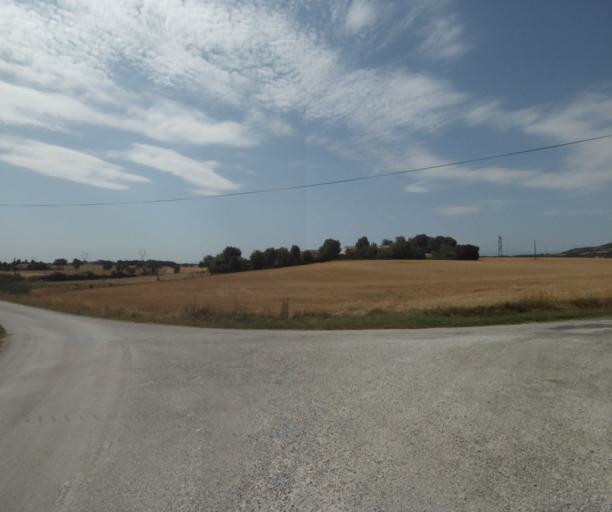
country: FR
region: Midi-Pyrenees
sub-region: Departement de la Haute-Garonne
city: Saint-Felix-Lauragais
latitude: 43.4262
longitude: 1.8982
